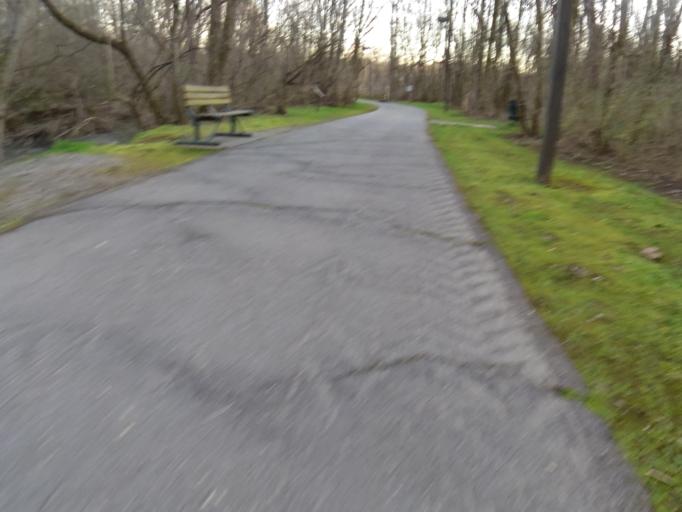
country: US
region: Tennessee
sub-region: Blount County
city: Maryville
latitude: 35.7625
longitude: -83.9825
